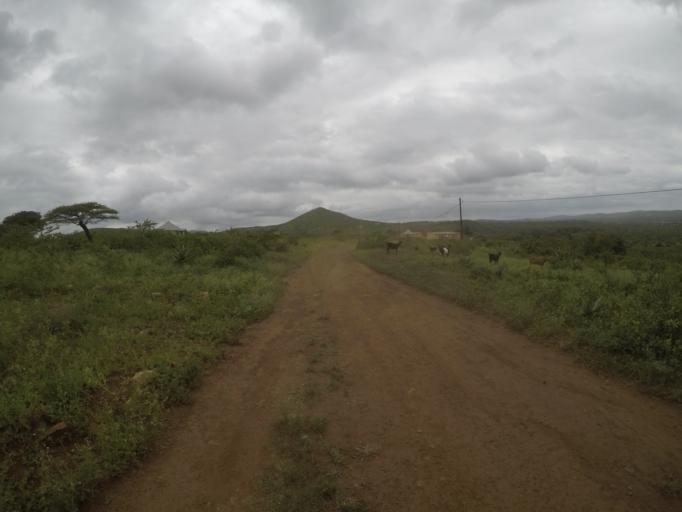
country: ZA
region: KwaZulu-Natal
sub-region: uThungulu District Municipality
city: Empangeni
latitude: -28.5869
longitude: 31.8627
